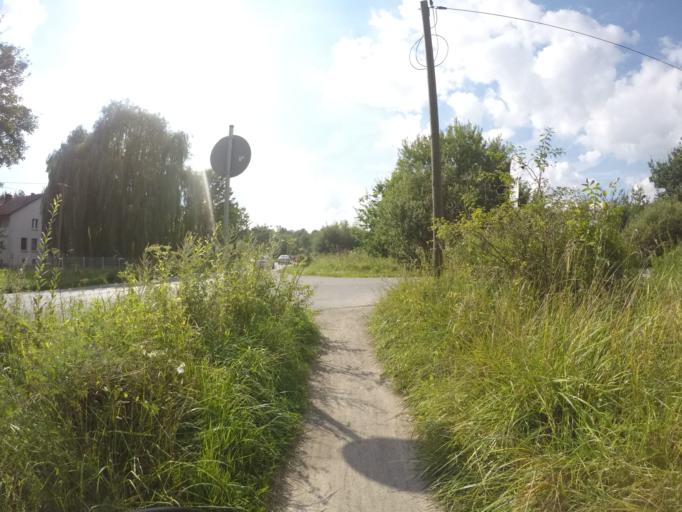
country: DE
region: North Rhine-Westphalia
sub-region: Regierungsbezirk Detmold
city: Bielefeld
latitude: 52.0534
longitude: 8.5733
